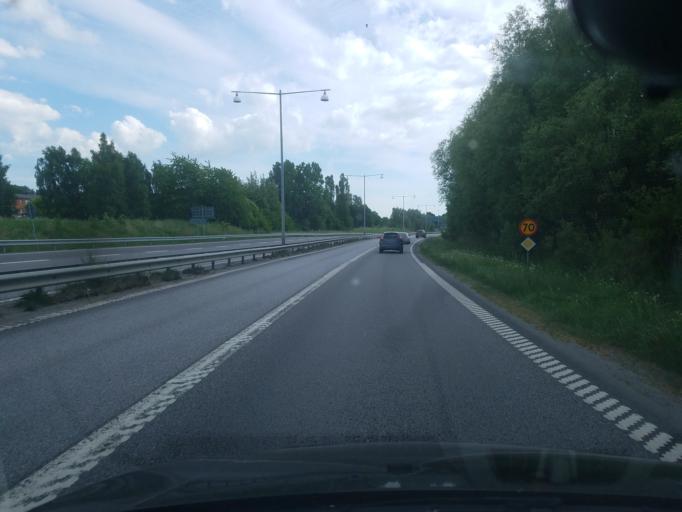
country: SE
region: Vaestra Goetaland
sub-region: Goteborg
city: Majorna
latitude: 57.6433
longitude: 11.9319
